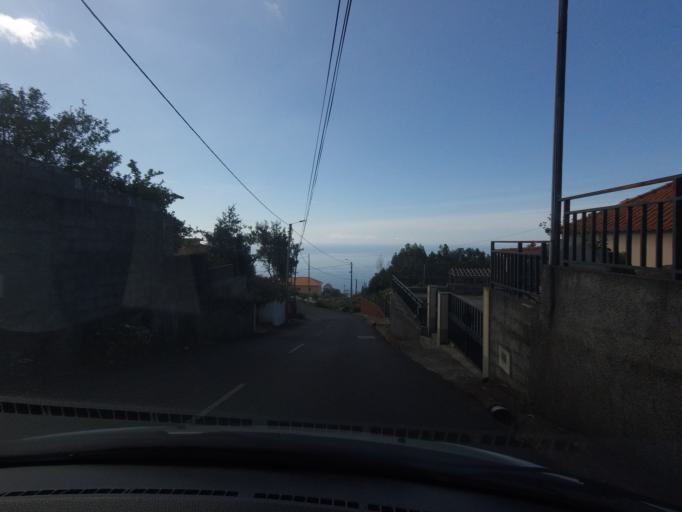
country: PT
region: Madeira
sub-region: Santa Cruz
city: Camacha
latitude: 32.6652
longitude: -16.8522
